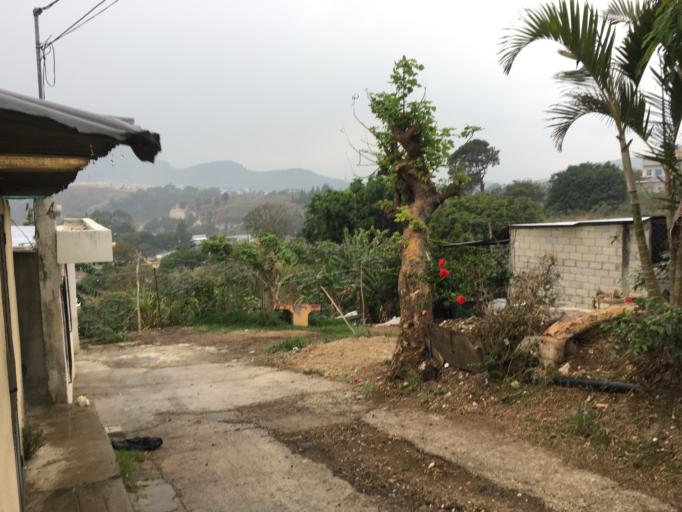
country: GT
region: Guatemala
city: Petapa
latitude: 14.5057
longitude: -90.5512
